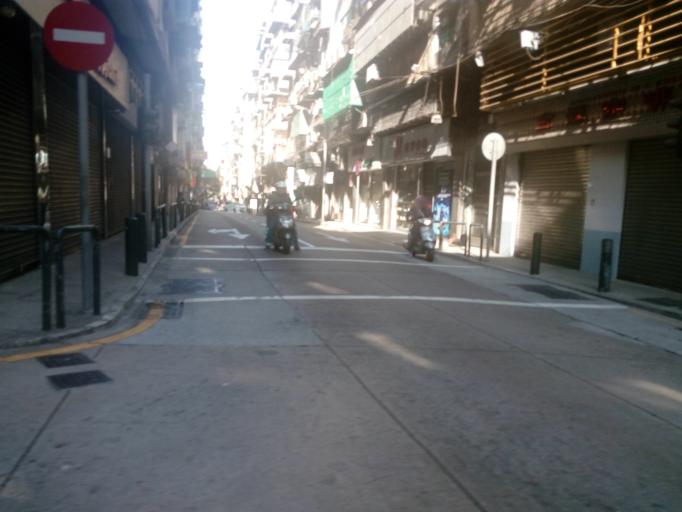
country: MO
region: Macau
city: Macau
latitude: 22.1994
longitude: 113.5462
